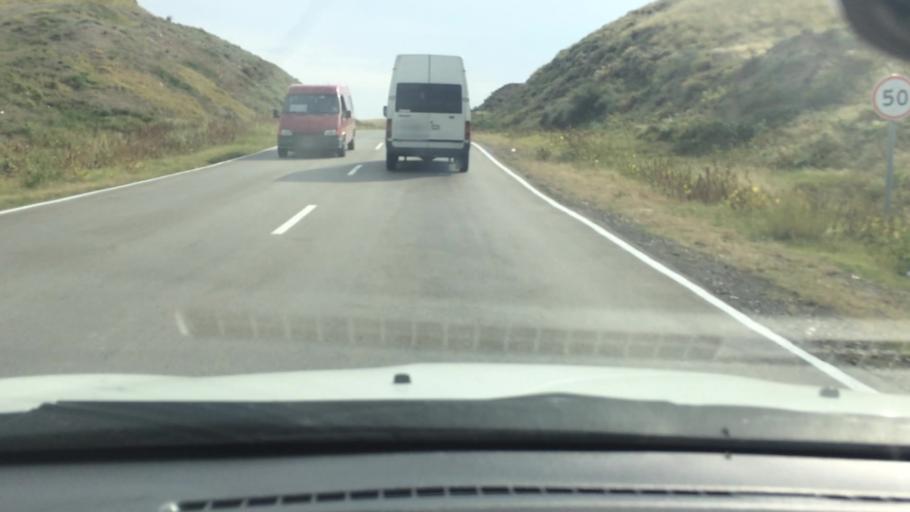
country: GE
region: Kvemo Kartli
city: Rust'avi
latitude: 41.5243
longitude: 44.9882
